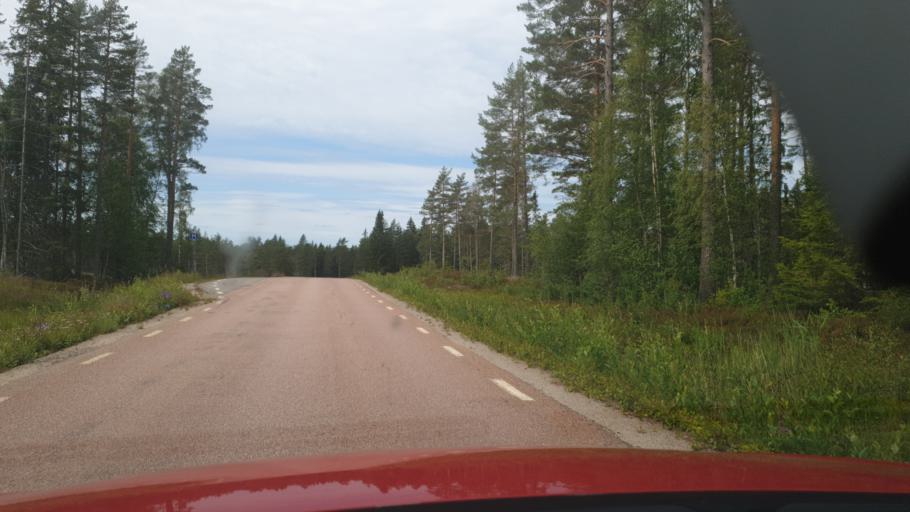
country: SE
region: Gaevleborg
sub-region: Hudiksvalls Kommun
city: Hudiksvall
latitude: 61.7013
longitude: 17.4098
